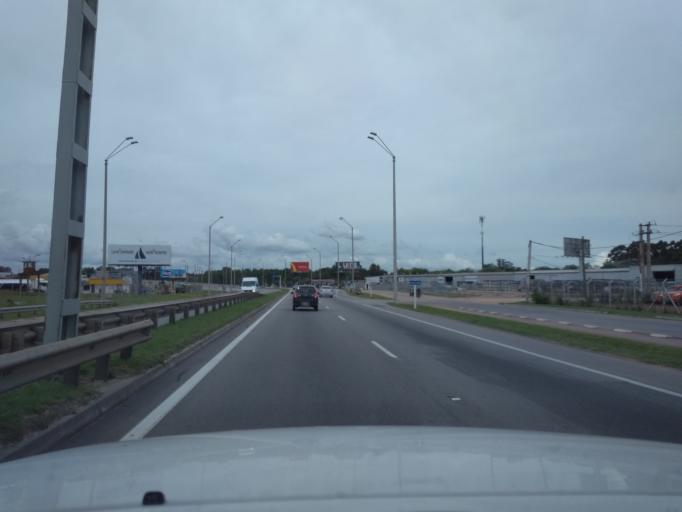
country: UY
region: Canelones
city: Barra de Carrasco
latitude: -34.8440
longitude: -56.0182
